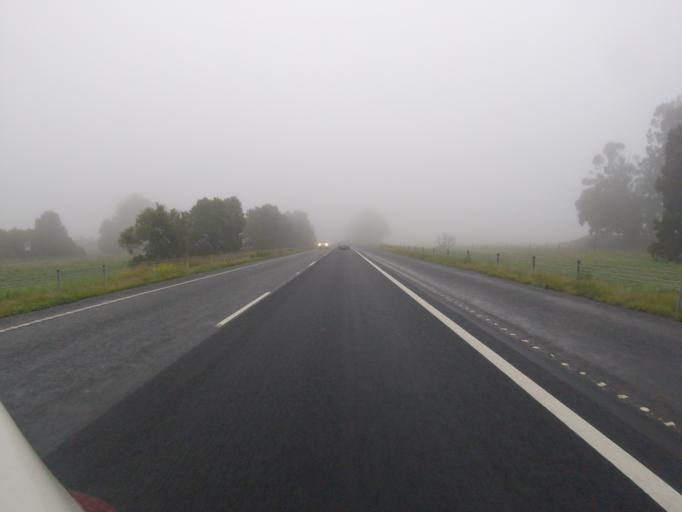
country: AU
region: Victoria
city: Brown Hill
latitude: -37.5496
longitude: 144.0323
